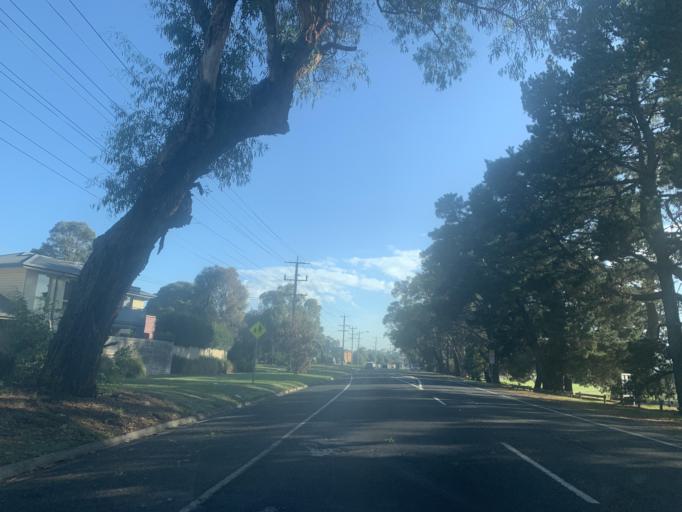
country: AU
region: Victoria
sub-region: Mornington Peninsula
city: Hastings
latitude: -38.3049
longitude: 145.1926
